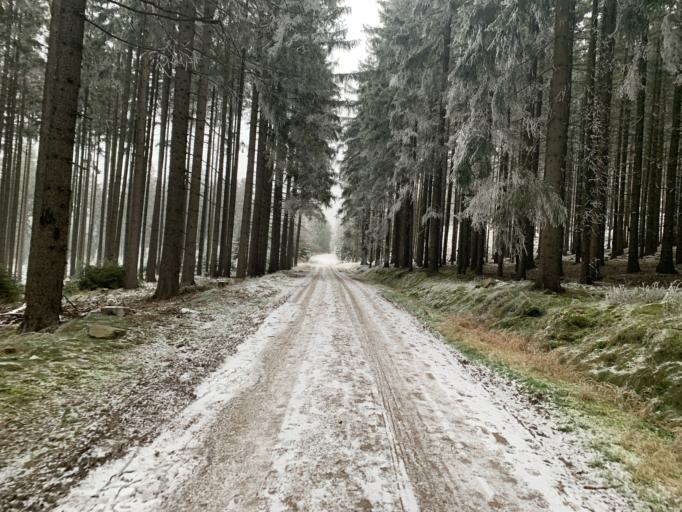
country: CZ
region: Central Bohemia
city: Rozmital pod Tremsinem
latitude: 49.5766
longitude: 13.8268
